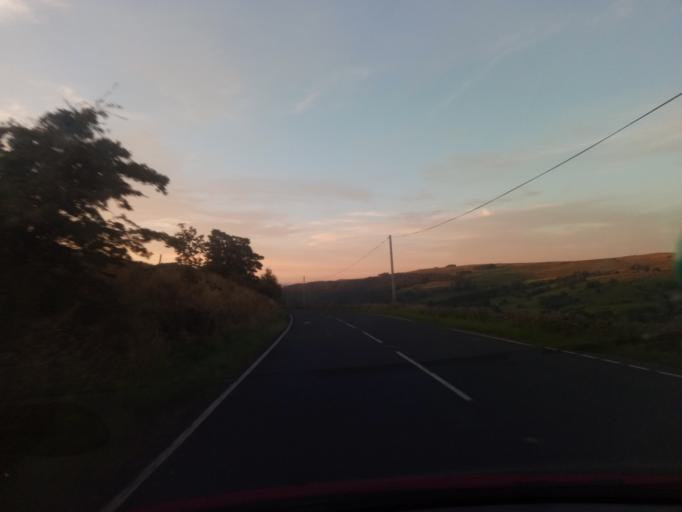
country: GB
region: England
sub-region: Northumberland
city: Bardon Mill
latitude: 54.8724
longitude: -2.3548
